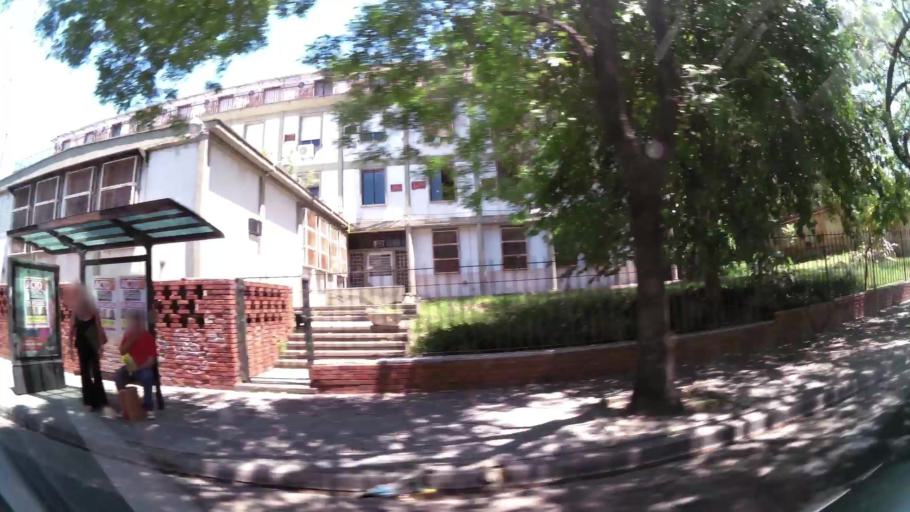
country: AR
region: Buenos Aires F.D.
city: Buenos Aires
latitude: -34.6379
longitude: -58.3816
